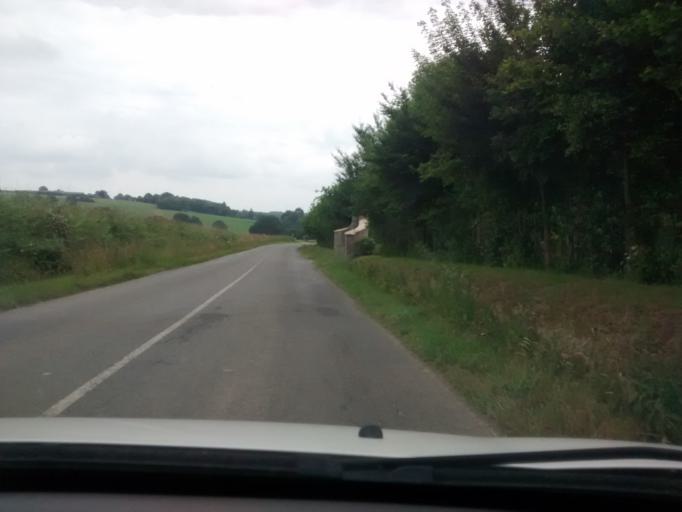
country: FR
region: Brittany
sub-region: Departement d'Ille-et-Vilaine
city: La Bouexiere
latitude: 48.1902
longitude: -1.4461
